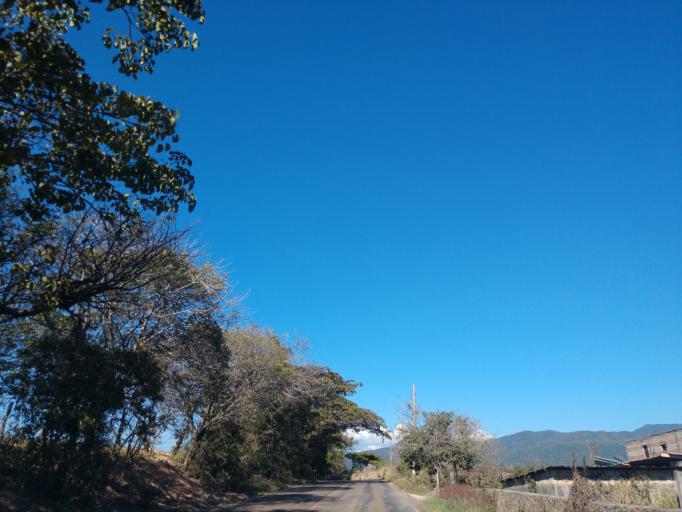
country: MX
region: Nayarit
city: Compostela
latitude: 21.2574
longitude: -104.8983
